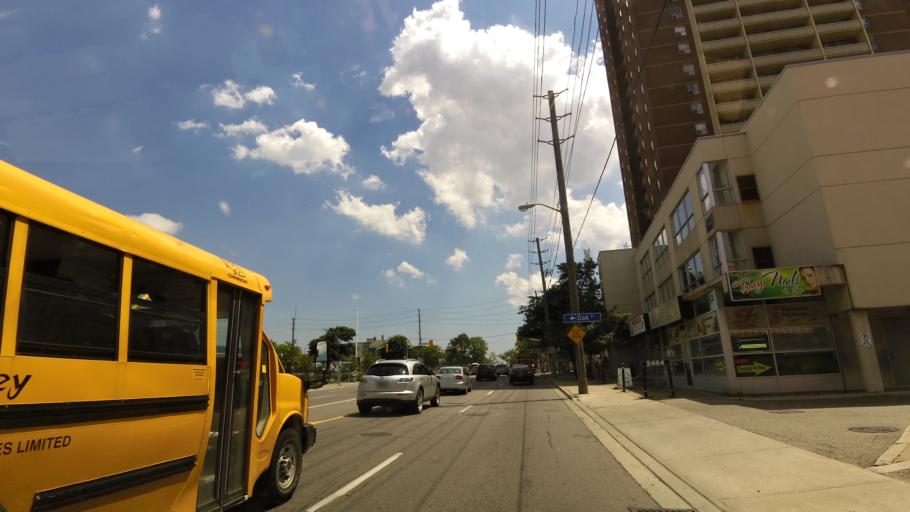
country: CA
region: Ontario
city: Etobicoke
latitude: 43.7085
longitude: -79.5340
